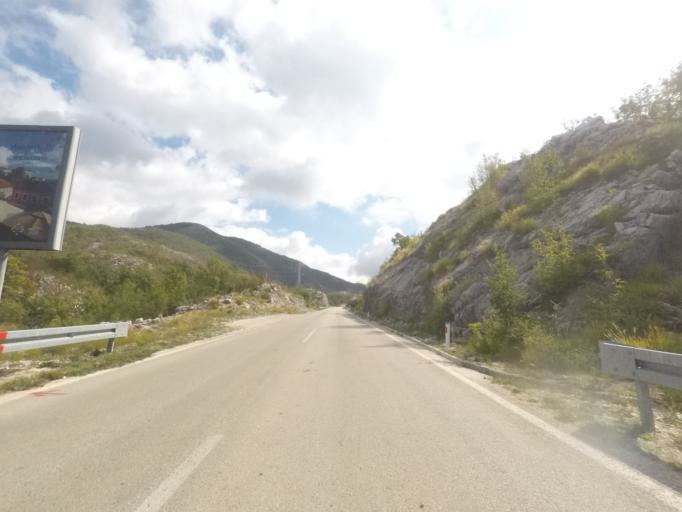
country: ME
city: Igalo
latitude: 42.5509
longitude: 18.4520
